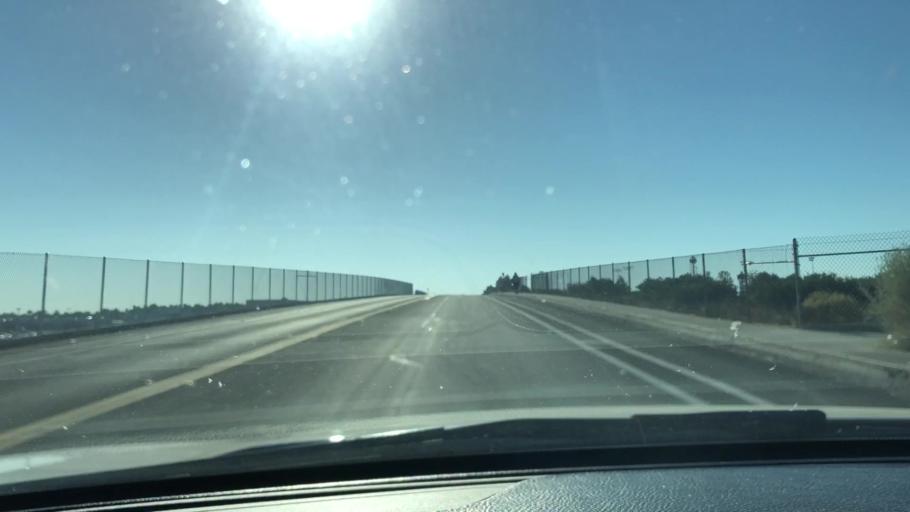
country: US
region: California
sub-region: Los Angeles County
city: Lancaster
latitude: 34.6676
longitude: -118.1554
